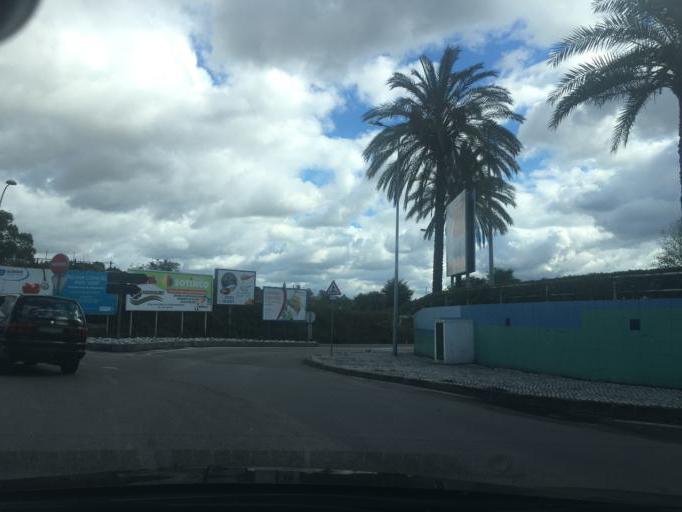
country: PT
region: Santarem
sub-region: Torres Novas
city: Torres Novas
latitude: 39.4656
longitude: -8.5243
